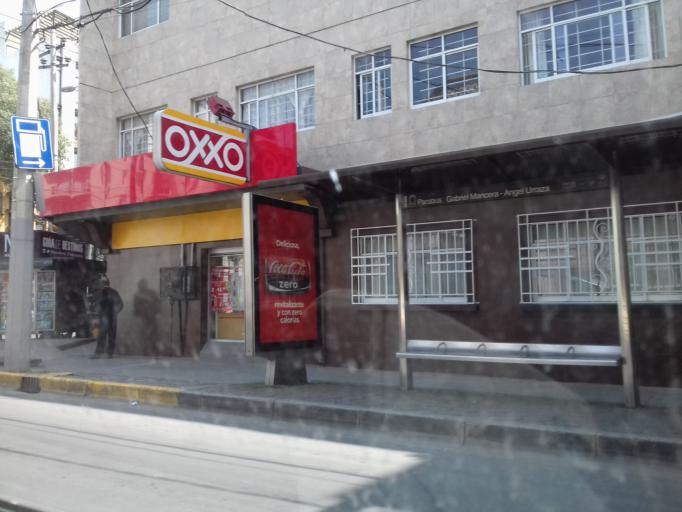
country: MX
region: Mexico City
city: Colonia del Valle
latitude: 19.3823
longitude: -99.1652
